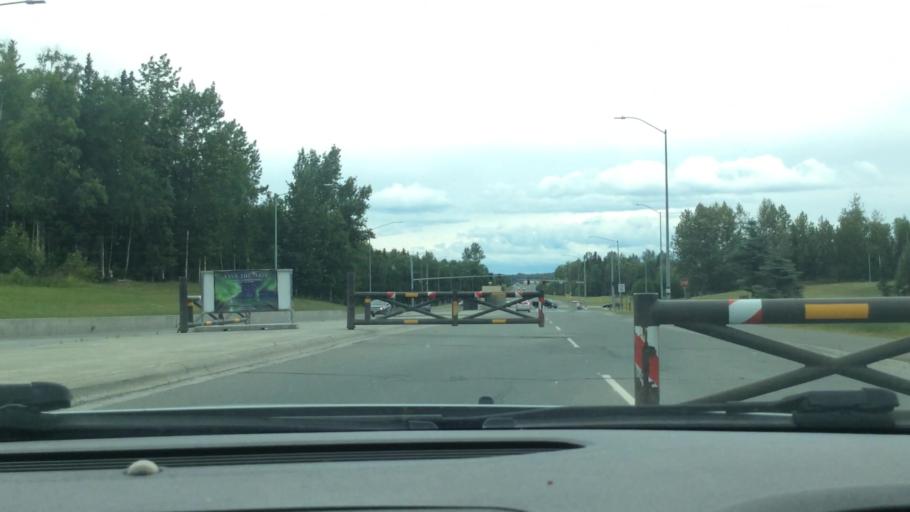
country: US
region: Alaska
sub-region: Anchorage Municipality
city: Anchorage
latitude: 61.2315
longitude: -149.7784
